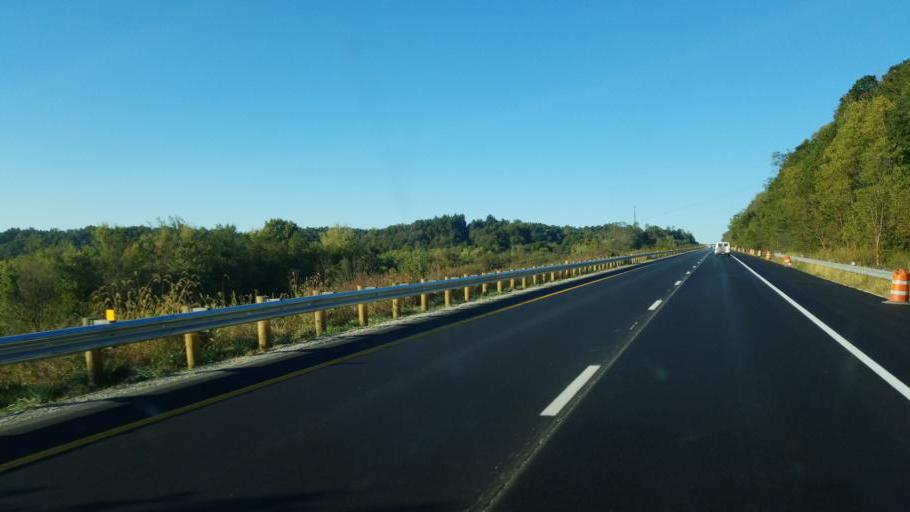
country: US
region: Ohio
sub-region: Guernsey County
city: Cambridge
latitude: 40.1107
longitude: -81.5612
